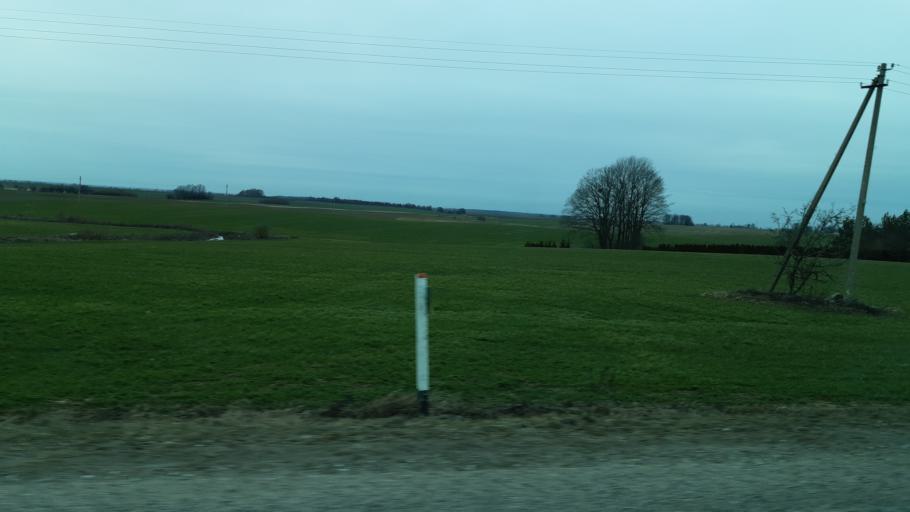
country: LT
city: Kybartai
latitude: 54.5516
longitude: 22.7232
